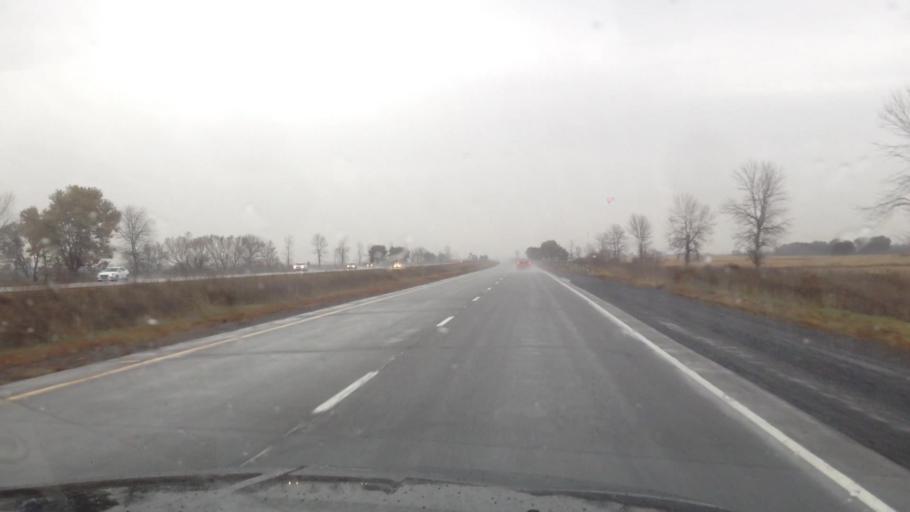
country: CA
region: Ontario
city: Casselman
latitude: 45.3158
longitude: -75.0229
